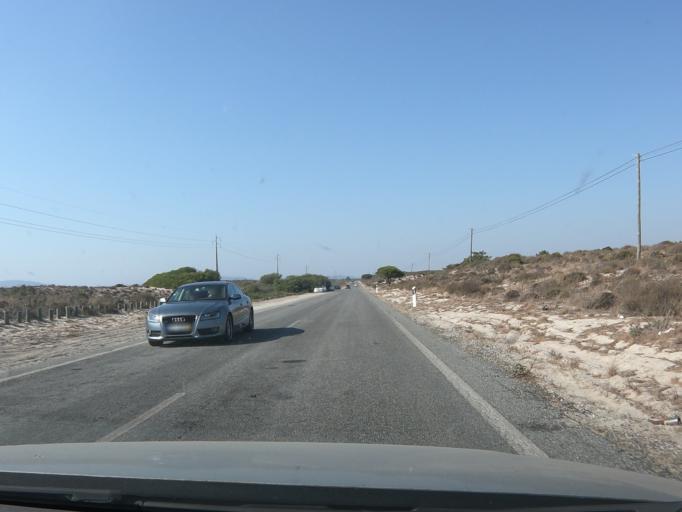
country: PT
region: Setubal
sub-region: Setubal
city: Setubal
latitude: 38.4255
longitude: -8.8237
